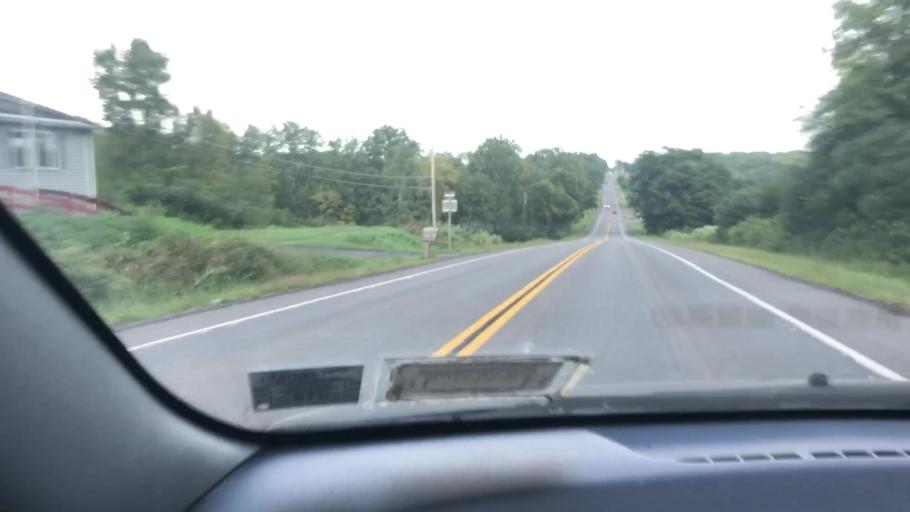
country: US
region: New York
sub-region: Wayne County
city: Macedon
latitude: 43.1392
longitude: -77.2898
